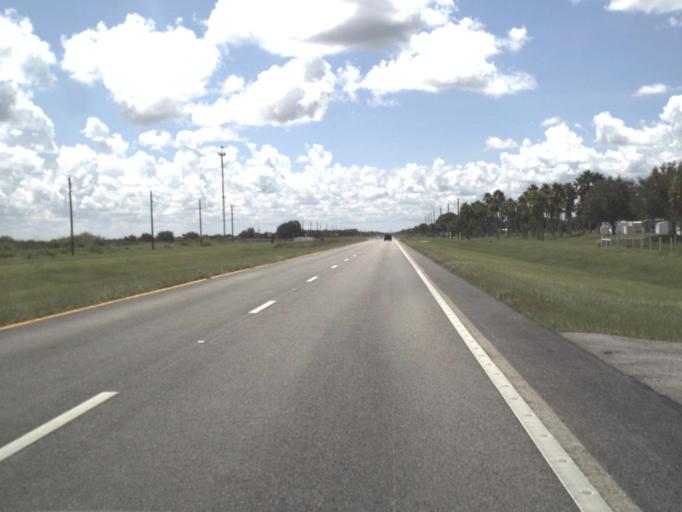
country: US
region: Florida
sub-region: Charlotte County
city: Harbour Heights
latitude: 27.0415
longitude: -81.9586
